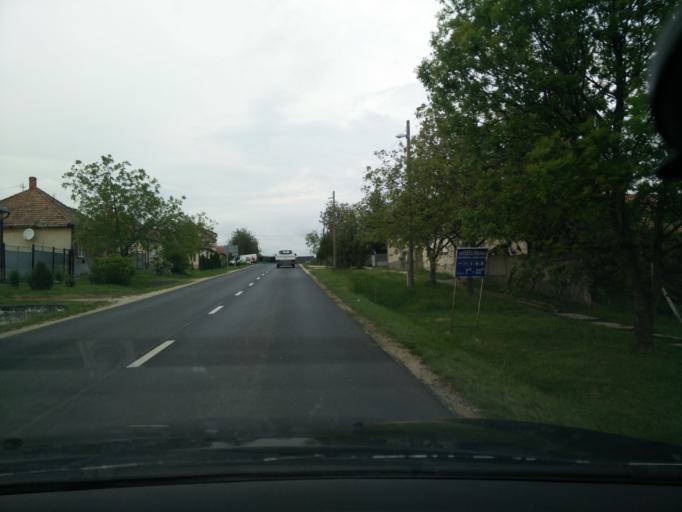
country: HU
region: Gyor-Moson-Sopron
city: Tet
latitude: 47.4647
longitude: 17.4896
